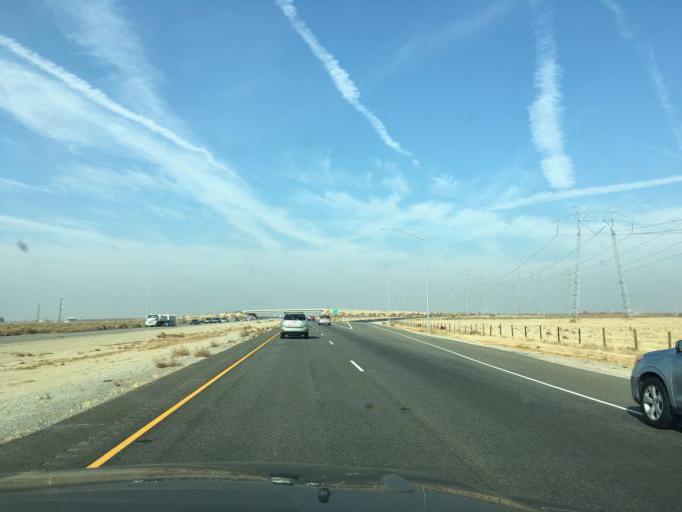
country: US
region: California
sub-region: Kern County
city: Buttonwillow
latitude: 35.4969
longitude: -119.5312
